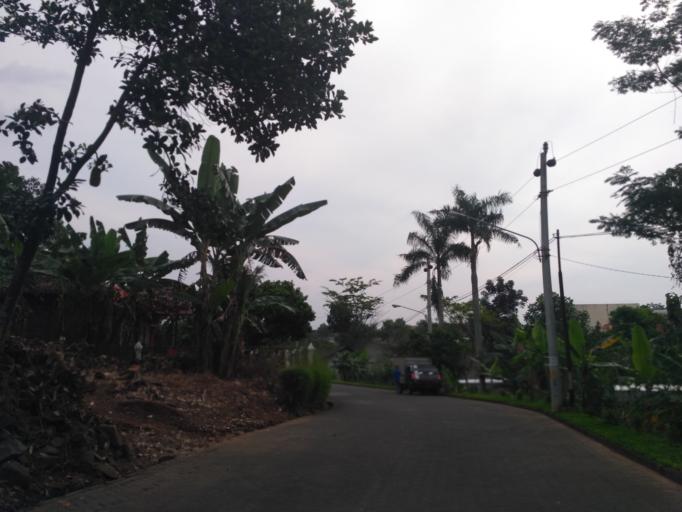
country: ID
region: Central Java
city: Ungaran
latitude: -7.0768
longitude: 110.4223
